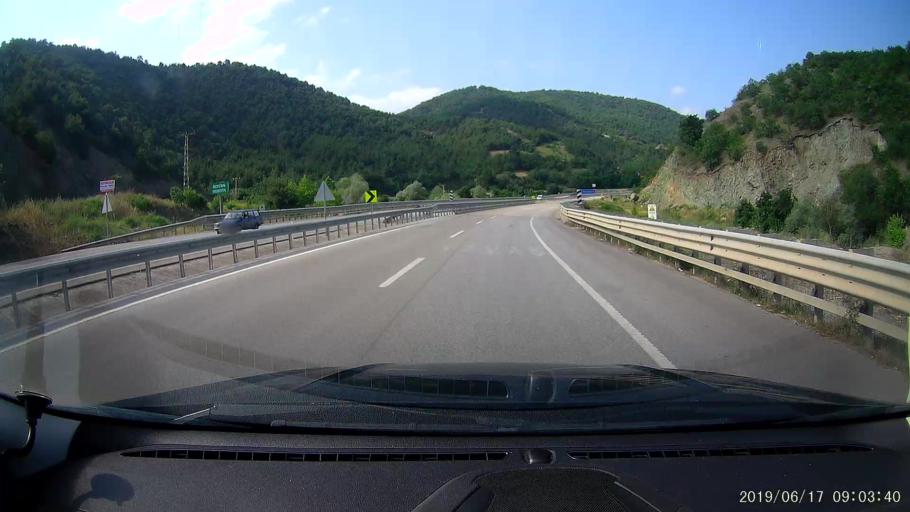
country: TR
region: Amasya
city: Tasova
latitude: 40.7520
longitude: 36.3021
